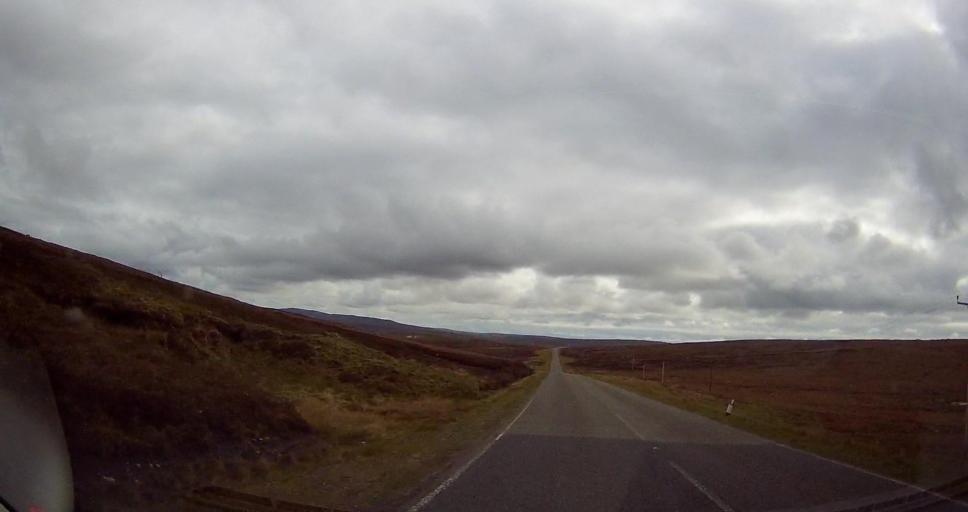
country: GB
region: Scotland
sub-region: Shetland Islands
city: Shetland
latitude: 60.6646
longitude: -1.0219
